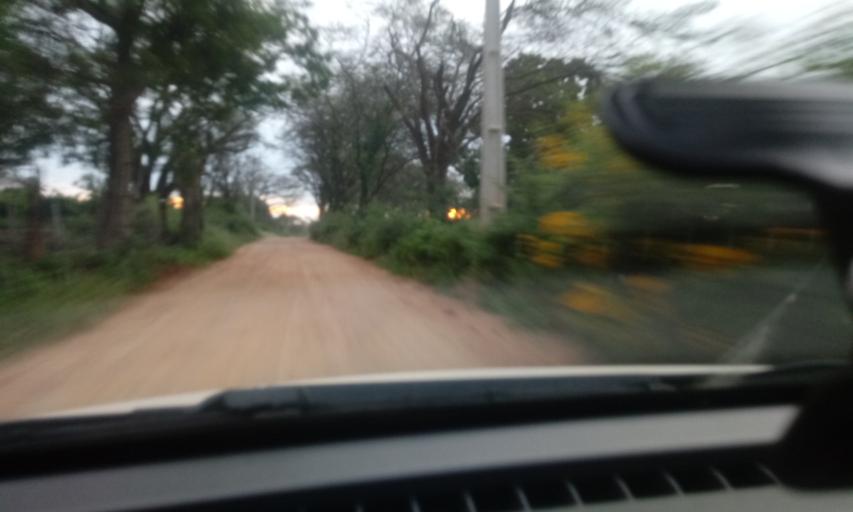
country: BR
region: Bahia
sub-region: Riacho De Santana
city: Riacho de Santana
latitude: -13.8010
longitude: -42.7482
